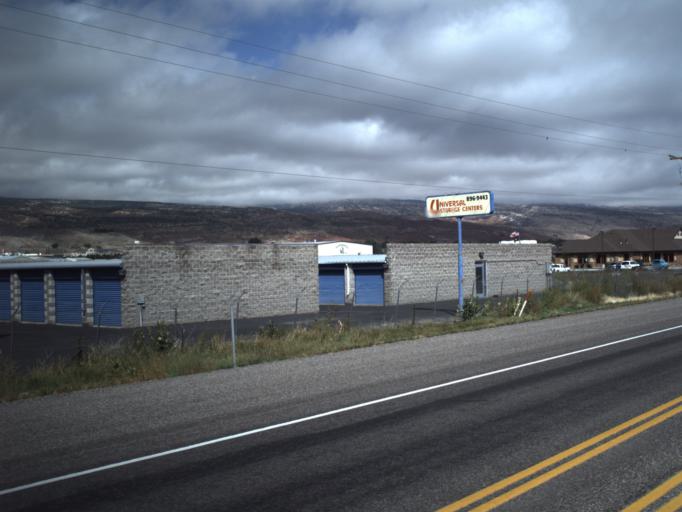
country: US
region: Utah
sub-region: Sevier County
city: Richfield
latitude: 38.7379
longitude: -112.0936
